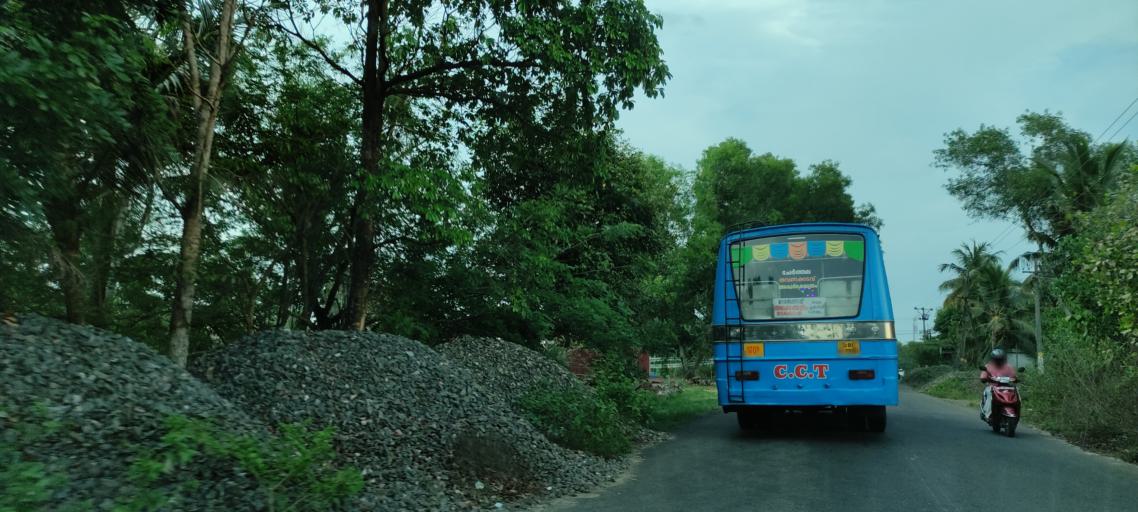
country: IN
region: Kerala
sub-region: Alappuzha
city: Kutiatodu
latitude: 9.7807
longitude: 76.3606
